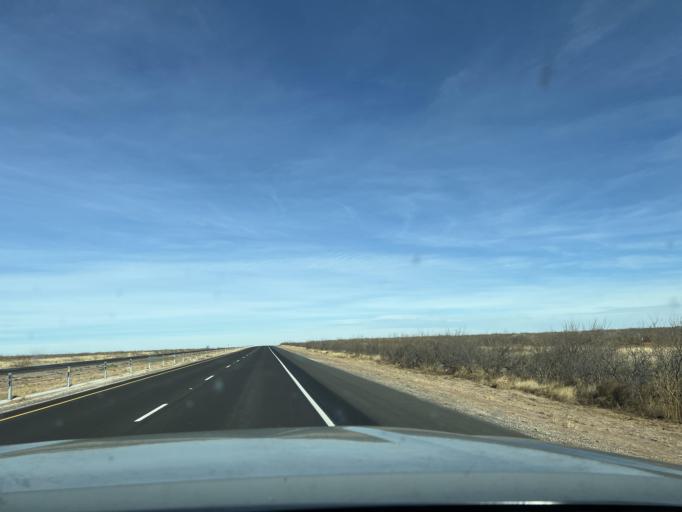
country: US
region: Texas
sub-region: Ector County
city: Gardendale
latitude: 32.0562
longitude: -102.4408
